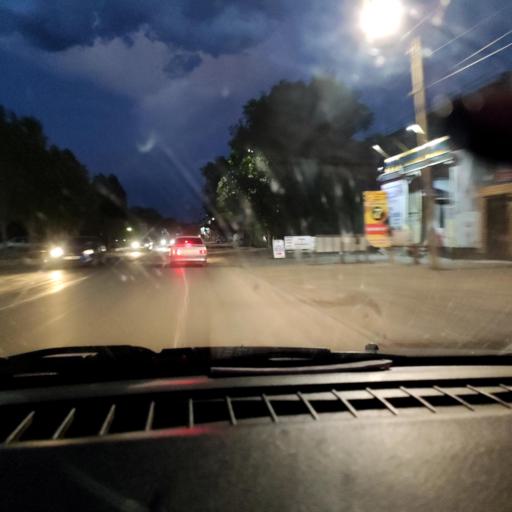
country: RU
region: Orenburg
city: Orenburg
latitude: 51.7999
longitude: 55.1437
